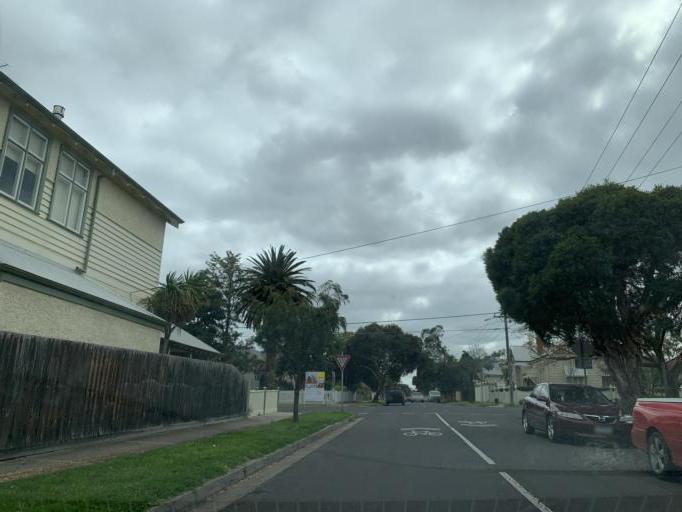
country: AU
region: Victoria
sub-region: Moreland
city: Pascoe Vale South
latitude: -37.7425
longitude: 144.9563
